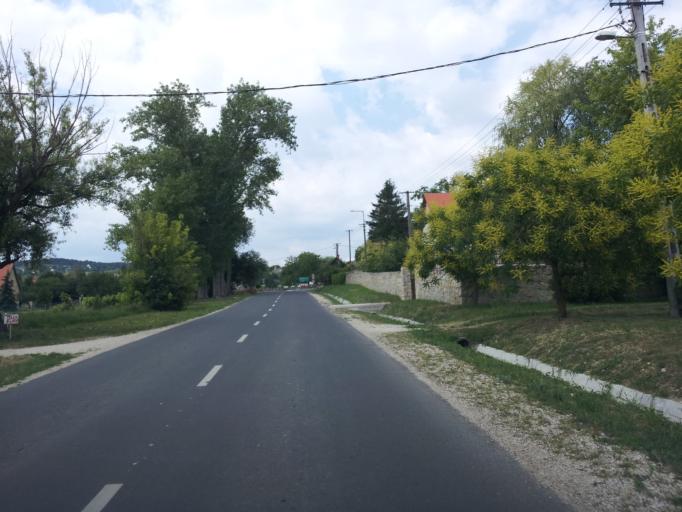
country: HU
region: Veszprem
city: Zanka
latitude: 46.9191
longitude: 17.7213
